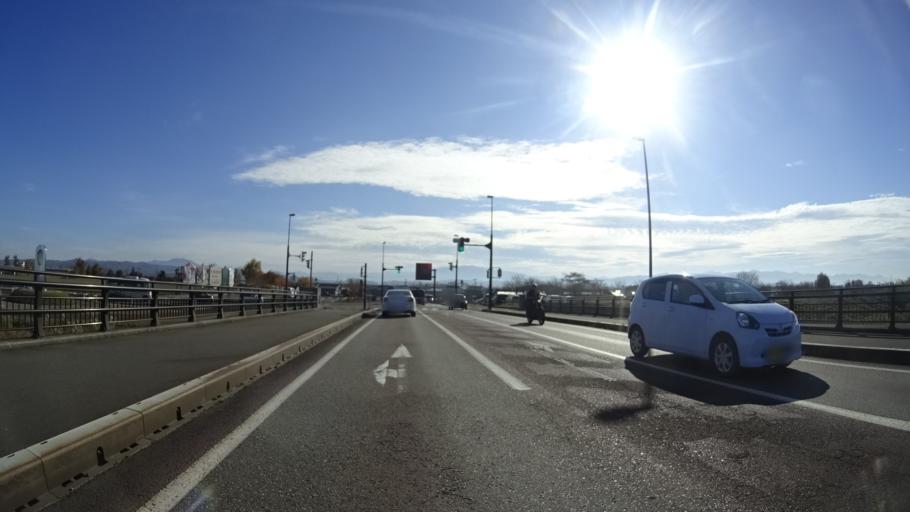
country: JP
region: Niigata
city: Mitsuke
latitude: 37.5453
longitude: 138.8826
